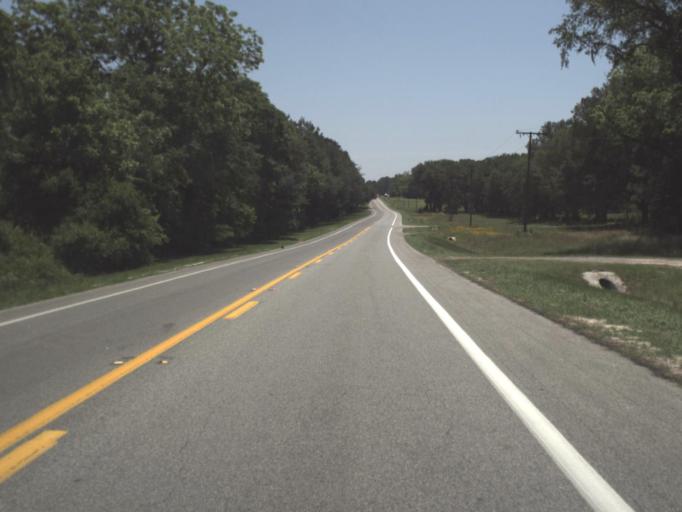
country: US
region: Florida
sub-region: Suwannee County
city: Live Oak
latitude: 30.3180
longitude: -83.0337
